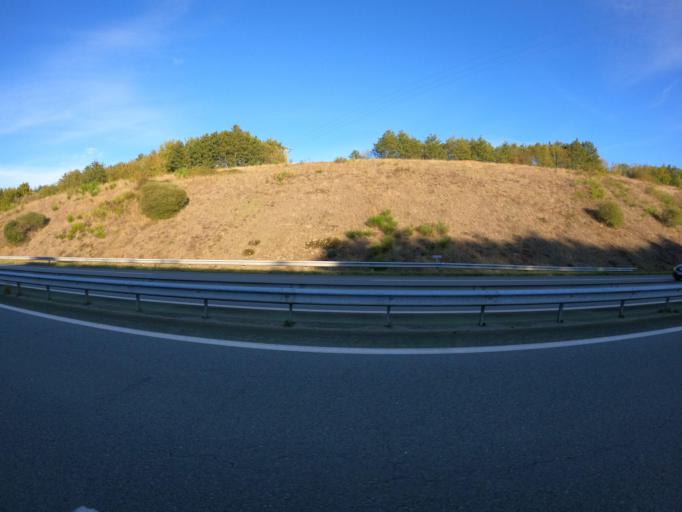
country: FR
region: Pays de la Loire
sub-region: Departement de Maine-et-Loire
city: Nuaille
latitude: 47.0928
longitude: -0.8241
